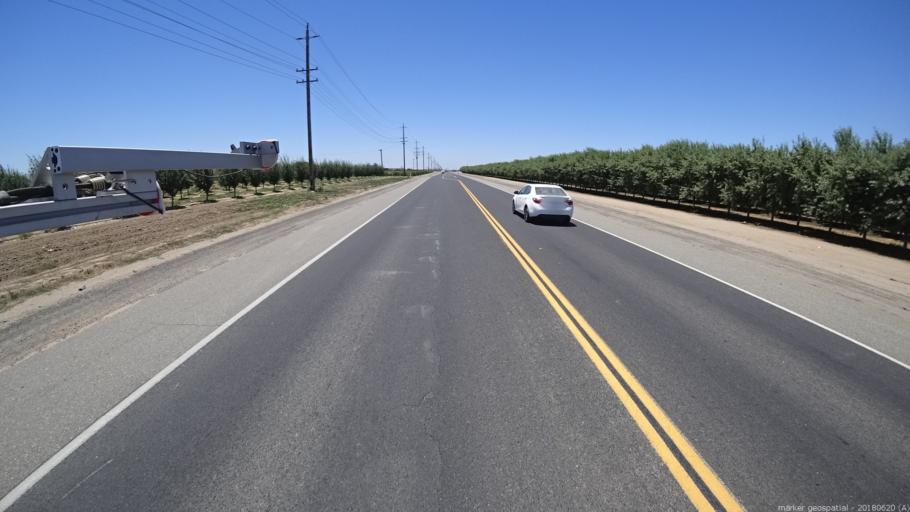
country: US
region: California
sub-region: Madera County
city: Parkwood
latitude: 36.9237
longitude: -120.0360
